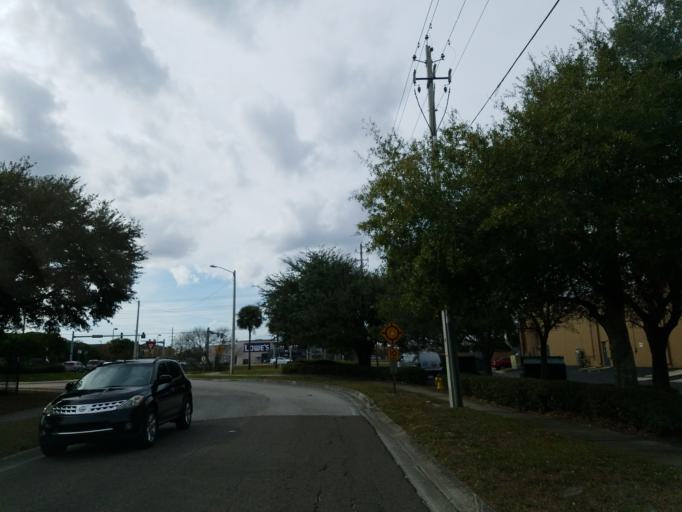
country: US
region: Florida
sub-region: Hillsborough County
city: Brandon
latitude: 27.9206
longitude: -82.3174
